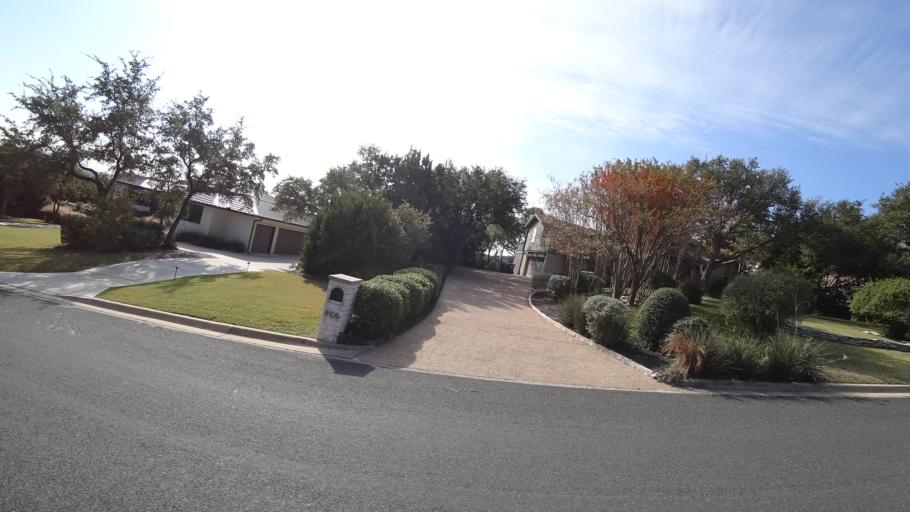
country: US
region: Texas
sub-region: Williamson County
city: Jollyville
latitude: 30.3757
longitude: -97.8105
